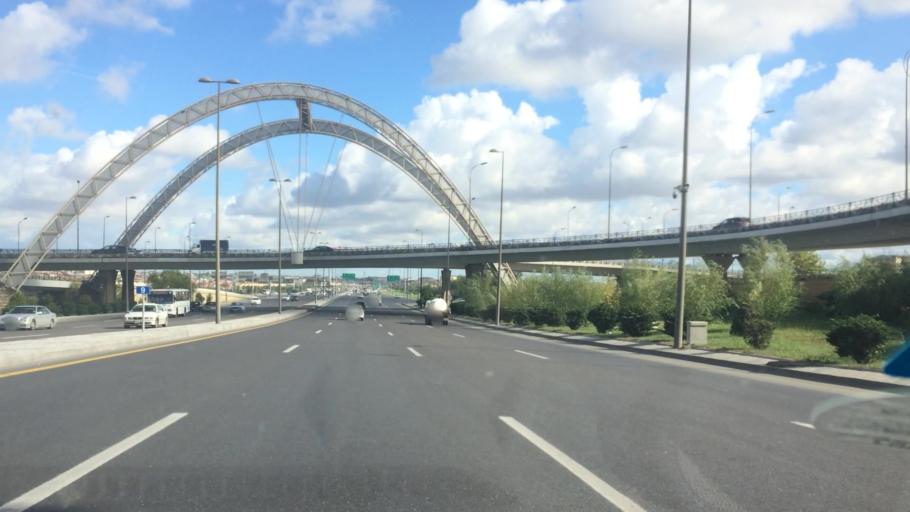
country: AZ
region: Baki
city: Sabuncu
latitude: 40.4245
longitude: 49.9209
